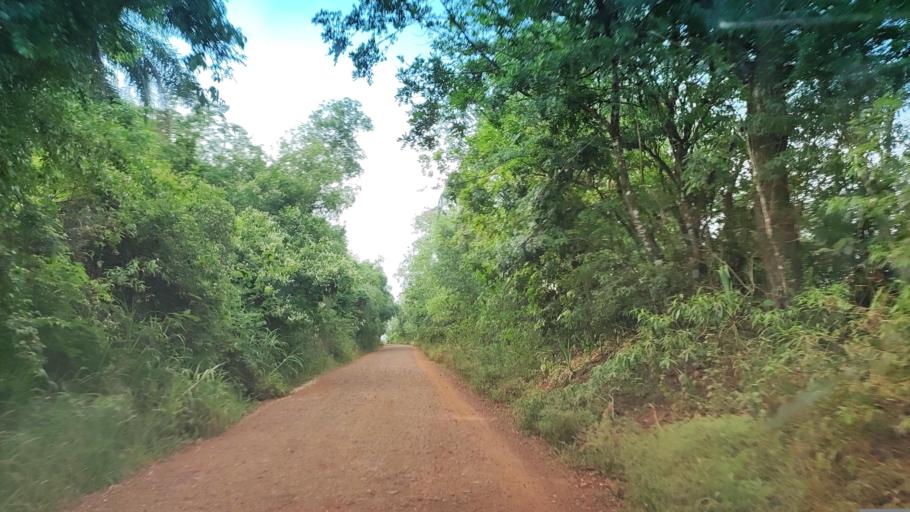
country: AR
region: Misiones
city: Gobernador Roca
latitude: -27.1707
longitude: -55.5084
